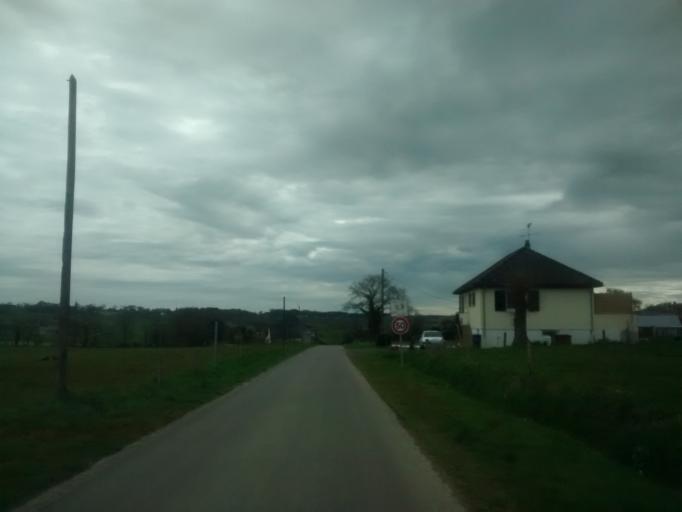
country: FR
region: Brittany
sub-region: Departement d'Ille-et-Vilaine
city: Gosne
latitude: 48.2397
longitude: -1.4880
